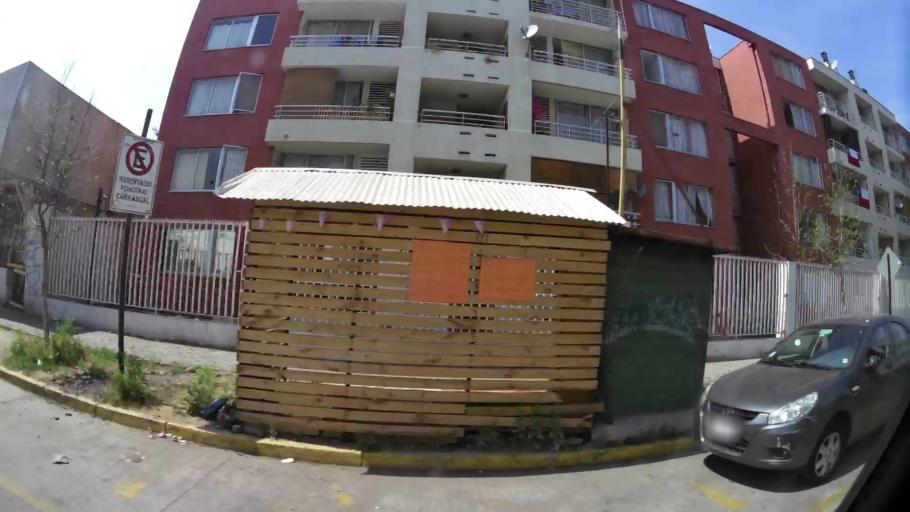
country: CL
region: Santiago Metropolitan
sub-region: Provincia de Santiago
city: Lo Prado
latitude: -33.4251
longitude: -70.6861
